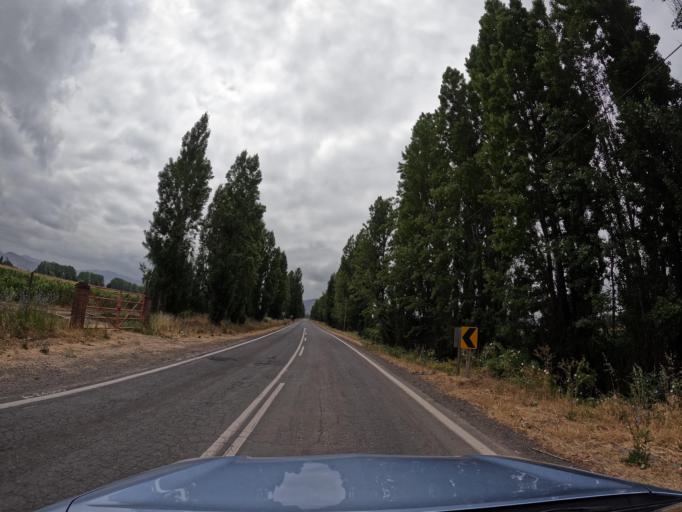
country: CL
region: Maule
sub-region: Provincia de Curico
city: Teno
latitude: -34.7517
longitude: -71.2240
